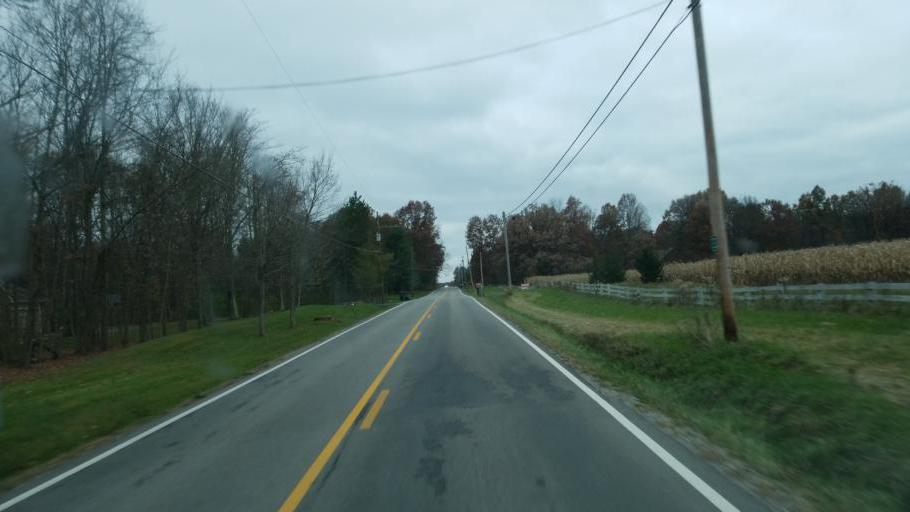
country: US
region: Ohio
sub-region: Delaware County
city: Sunbury
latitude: 40.1887
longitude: -82.8604
